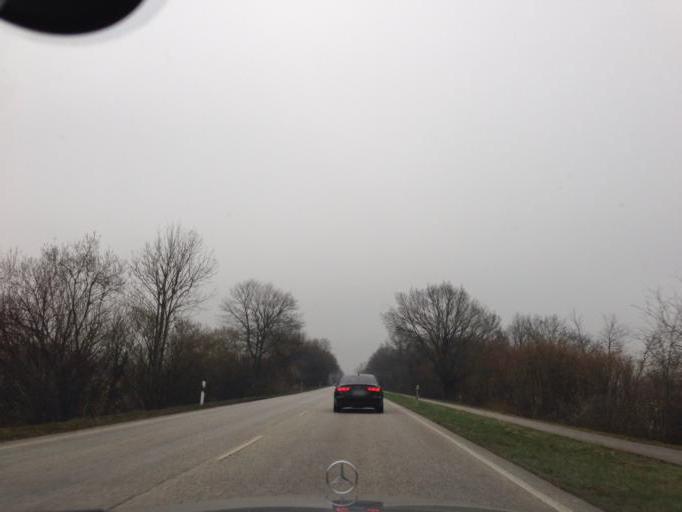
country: DE
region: Schleswig-Holstein
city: Warnau
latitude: 54.1971
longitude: 10.1565
